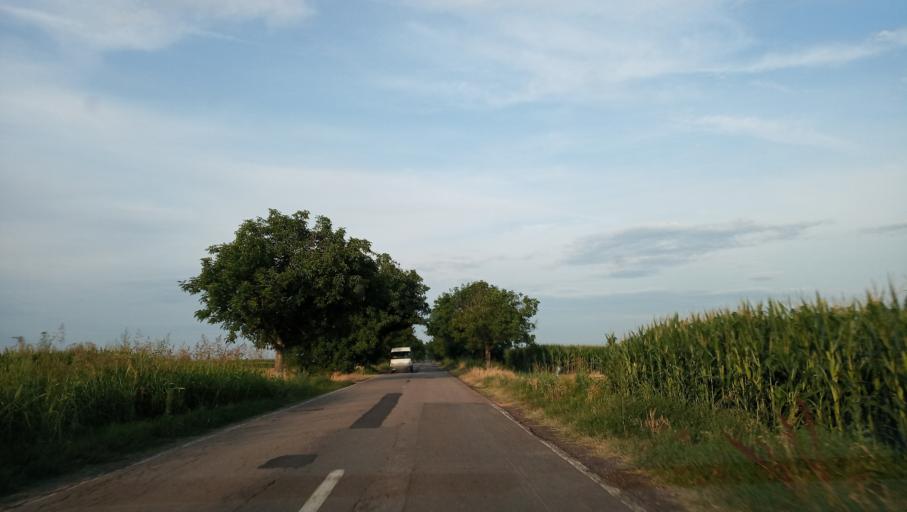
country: RO
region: Giurgiu
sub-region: Comuna Greaca
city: Greaca
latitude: 44.1037
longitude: 26.2936
